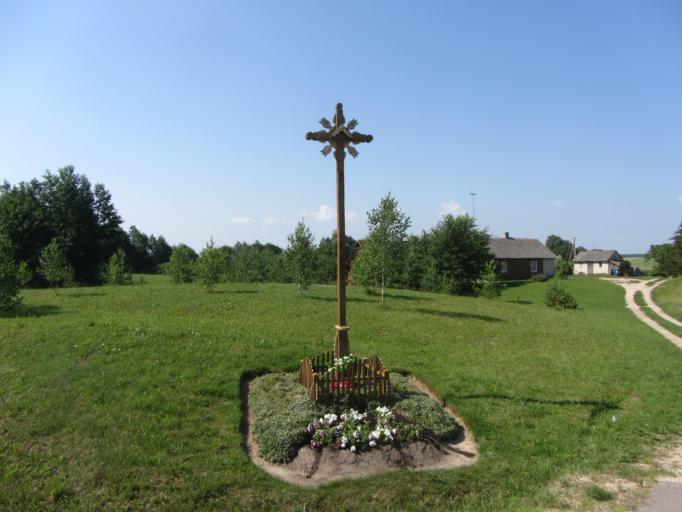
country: LT
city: Lazdijai
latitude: 54.2269
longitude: 23.6437
